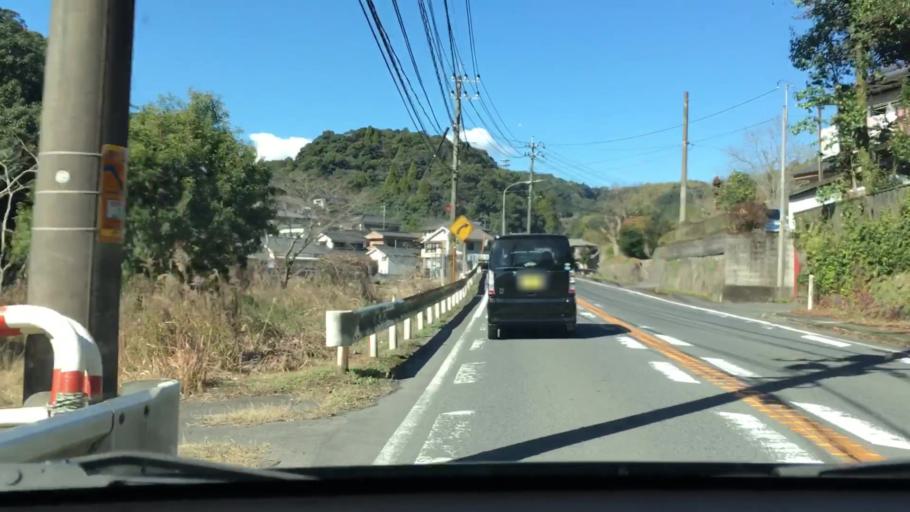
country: JP
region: Kagoshima
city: Kagoshima-shi
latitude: 31.6493
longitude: 130.5132
